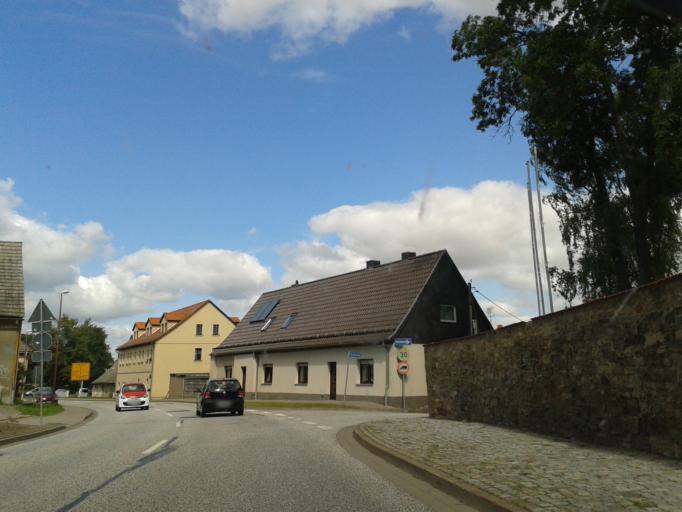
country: DE
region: Saxony-Anhalt
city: Klostermansfeld
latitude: 51.5830
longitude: 11.4971
